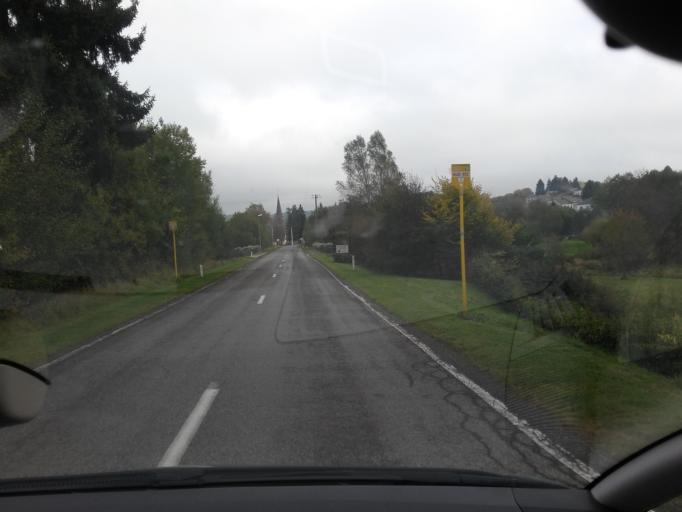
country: BE
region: Wallonia
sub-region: Province du Luxembourg
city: Chiny
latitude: 49.7632
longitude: 5.3949
